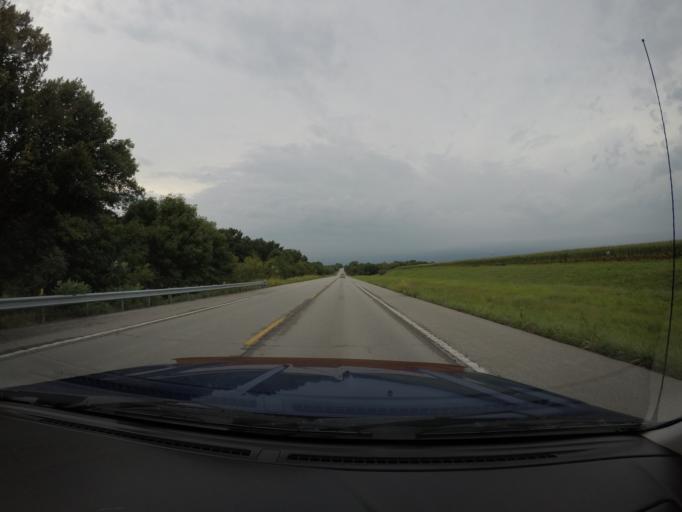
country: US
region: Missouri
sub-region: Ray County
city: Albany
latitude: 39.1158
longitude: -94.0548
